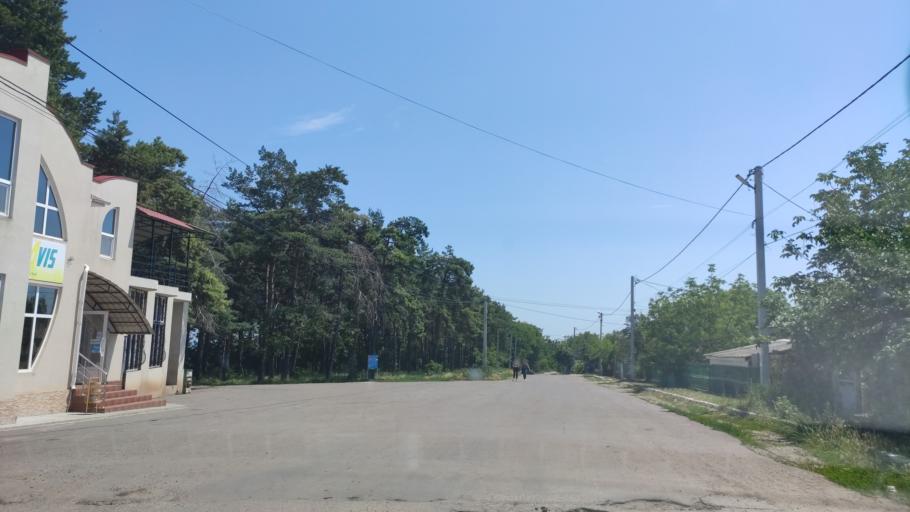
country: MD
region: Raionul Soroca
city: Soroca
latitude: 48.1453
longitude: 28.2893
